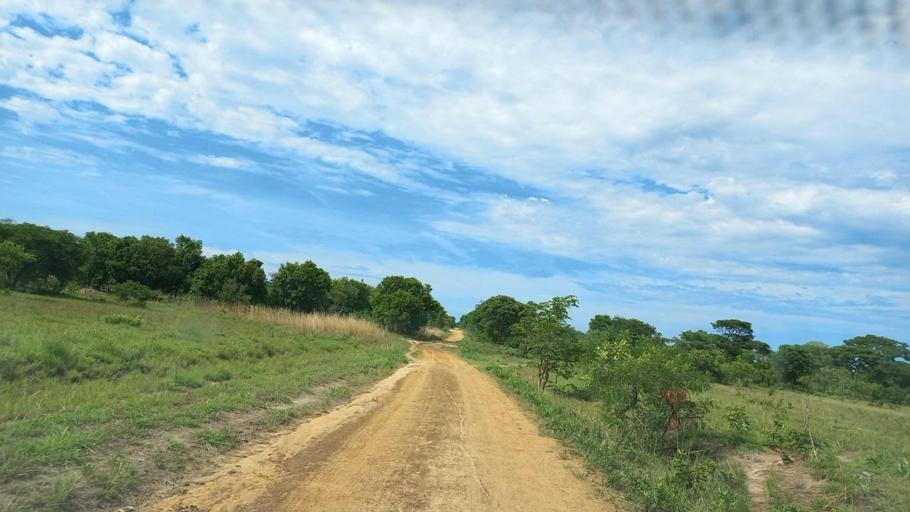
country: ZM
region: North-Western
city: Kabompo
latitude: -13.5161
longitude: 24.3889
